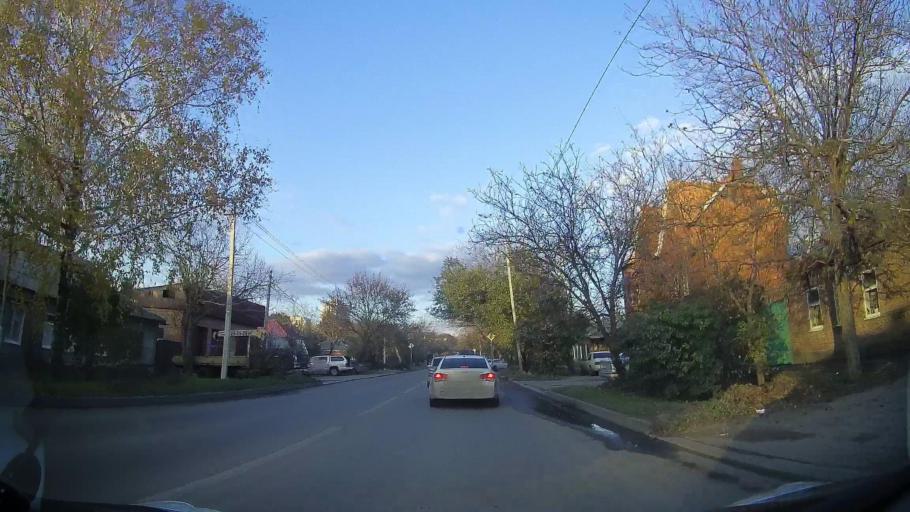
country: RU
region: Rostov
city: Imeni Chkalova
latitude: 47.2698
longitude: 39.7795
